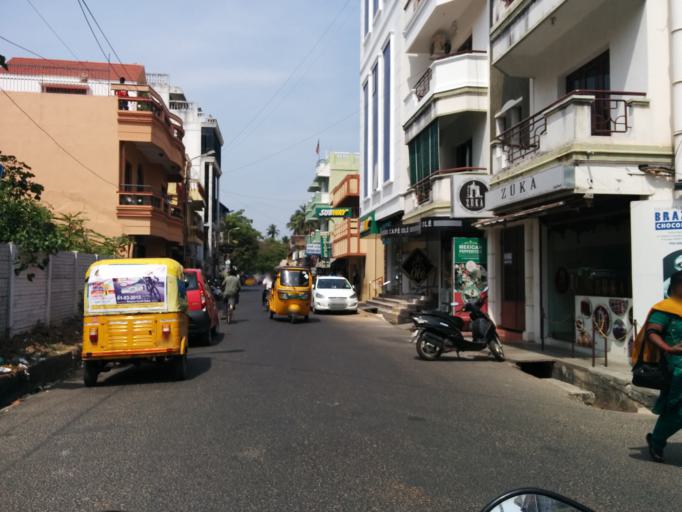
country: IN
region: Pondicherry
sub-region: Puducherry
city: Puducherry
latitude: 11.9297
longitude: 79.8302
